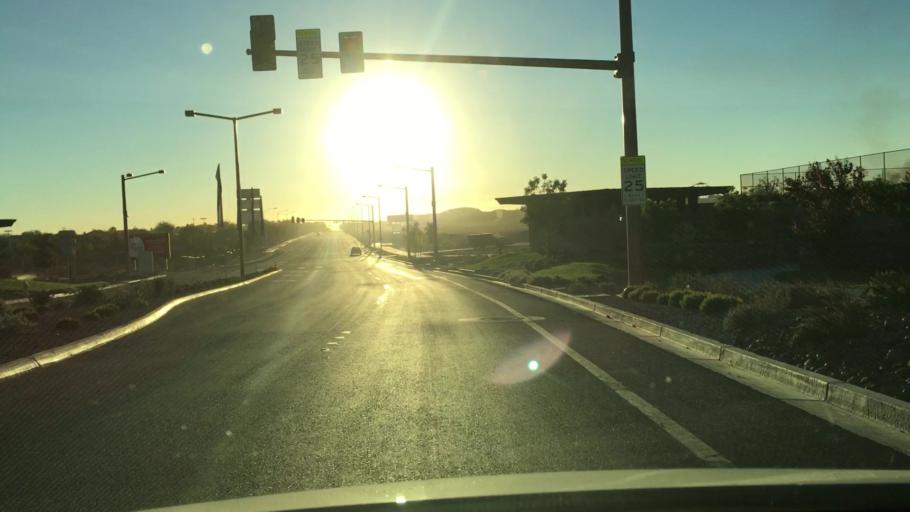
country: US
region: Nevada
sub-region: Clark County
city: Summerlin South
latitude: 36.0627
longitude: -115.3080
